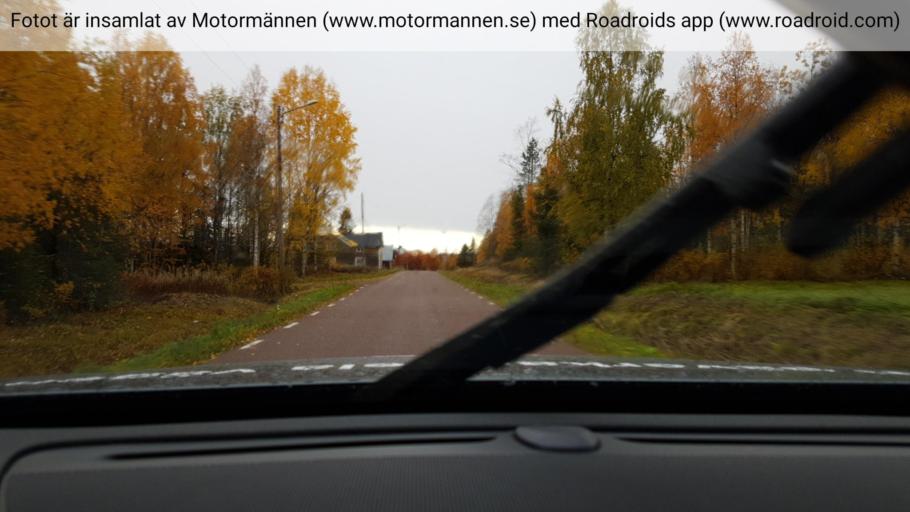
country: SE
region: Norrbotten
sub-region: Pajala Kommun
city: Pajala
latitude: 66.9613
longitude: 22.9456
